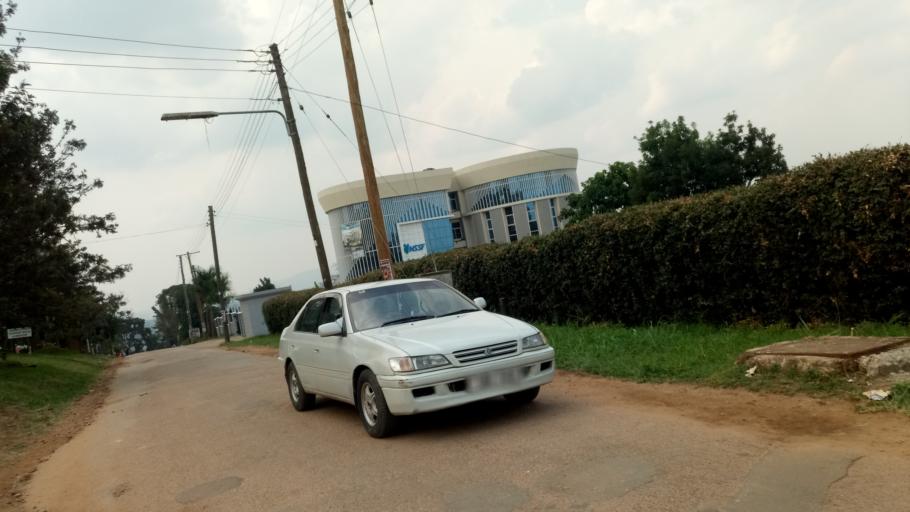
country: UG
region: Western Region
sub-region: Mbarara District
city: Mbarara
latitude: -0.6107
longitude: 30.6593
